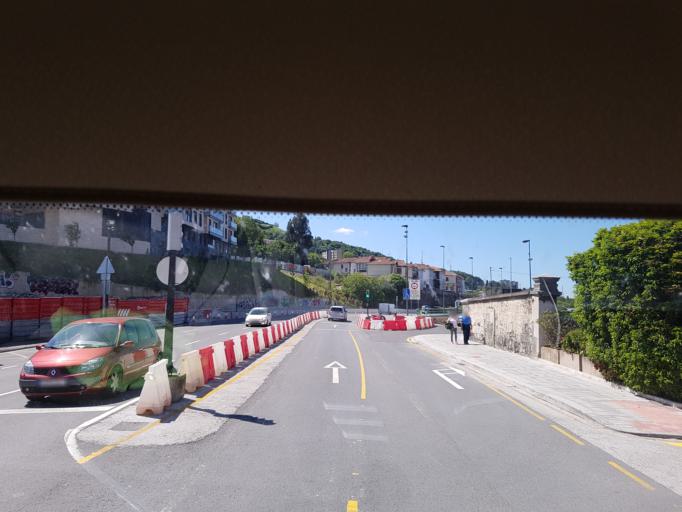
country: ES
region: Basque Country
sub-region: Bizkaia
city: Bilbao
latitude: 43.2604
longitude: -2.9542
